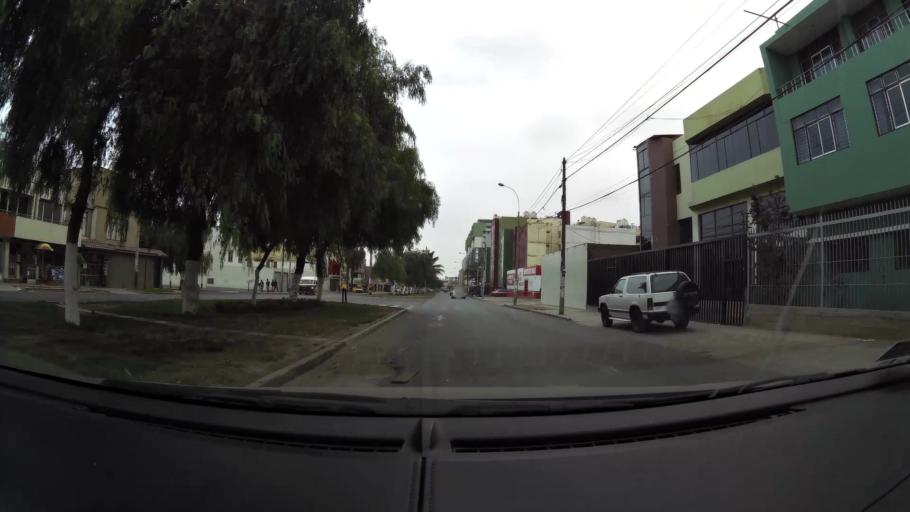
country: PE
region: La Libertad
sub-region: Provincia de Trujillo
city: Trujillo
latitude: -8.0948
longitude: -79.0270
